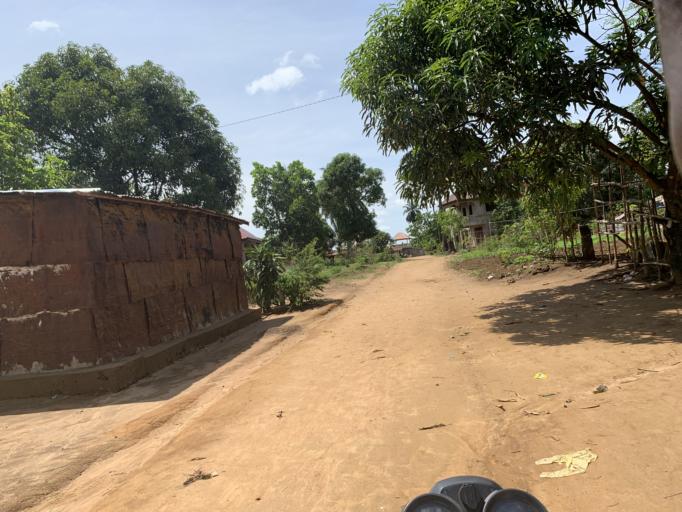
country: SL
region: Western Area
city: Waterloo
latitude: 8.3390
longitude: -13.0505
